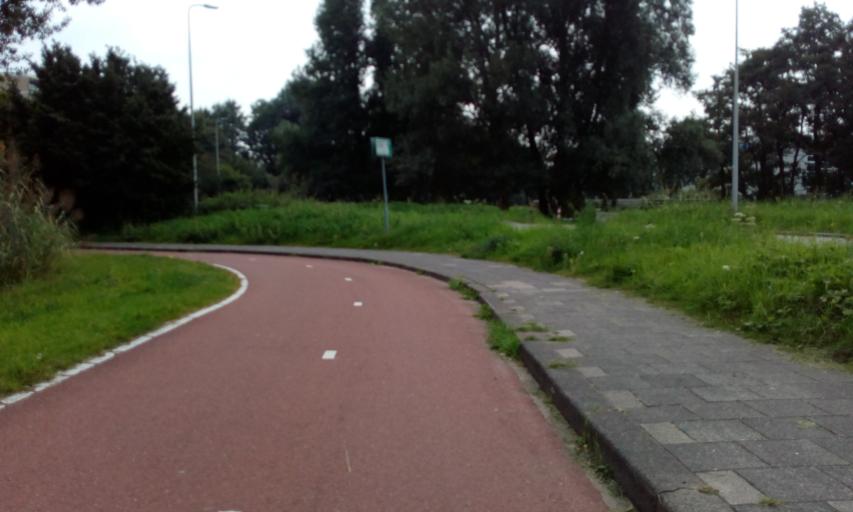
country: NL
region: South Holland
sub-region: Gemeente Rotterdam
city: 's-Gravenland
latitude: 51.9370
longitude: 4.5627
